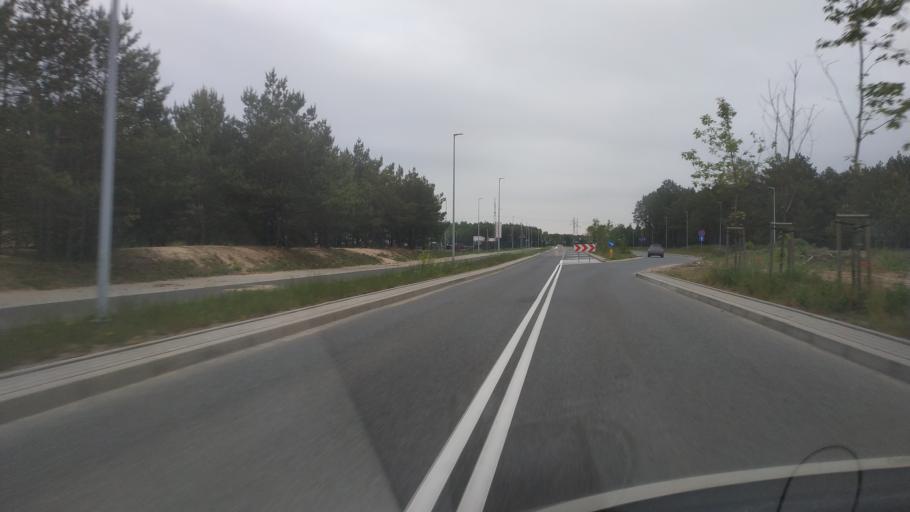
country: PL
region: Kujawsko-Pomorskie
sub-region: Powiat torunski
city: Lysomice
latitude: 53.0525
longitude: 18.6113
